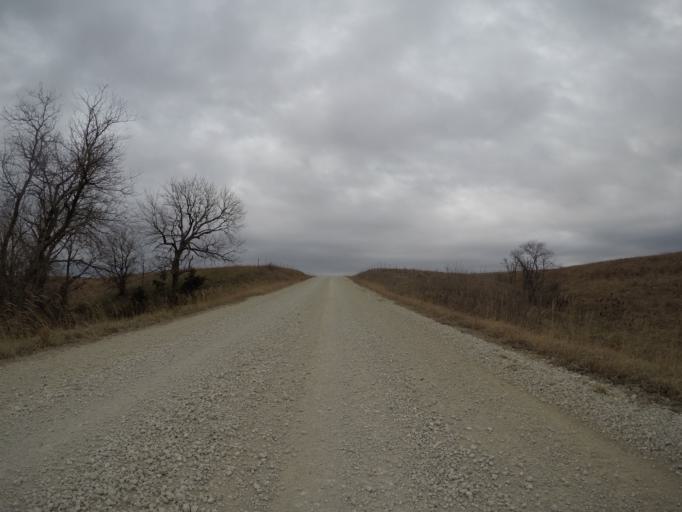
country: US
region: Kansas
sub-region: Wabaunsee County
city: Alma
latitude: 38.7694
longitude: -96.1497
